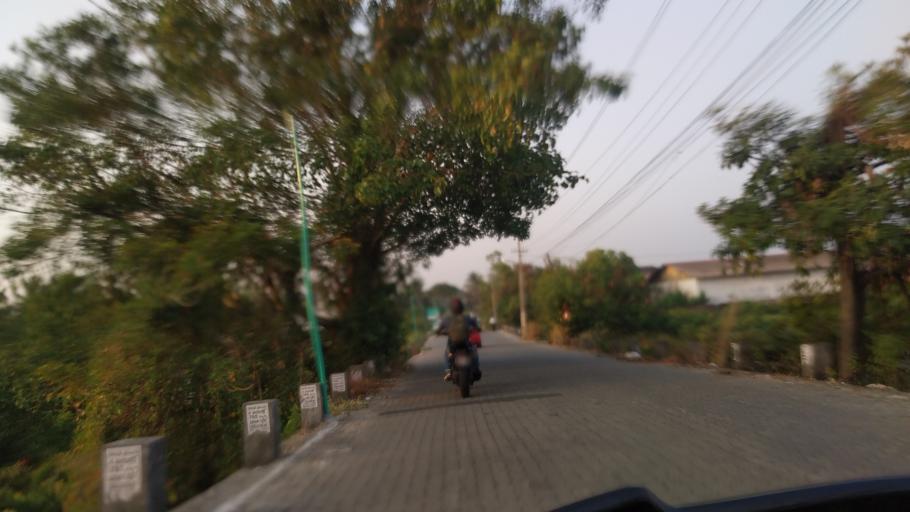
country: IN
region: Kerala
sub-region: Ernakulam
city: Elur
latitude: 10.0404
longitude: 76.2747
